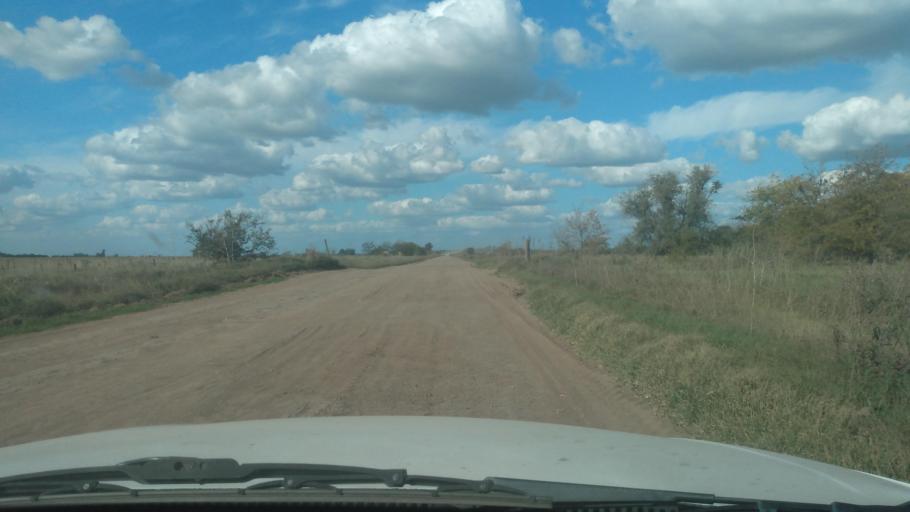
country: AR
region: Buenos Aires
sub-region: Partido de Navarro
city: Navarro
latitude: -35.0113
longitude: -59.4259
